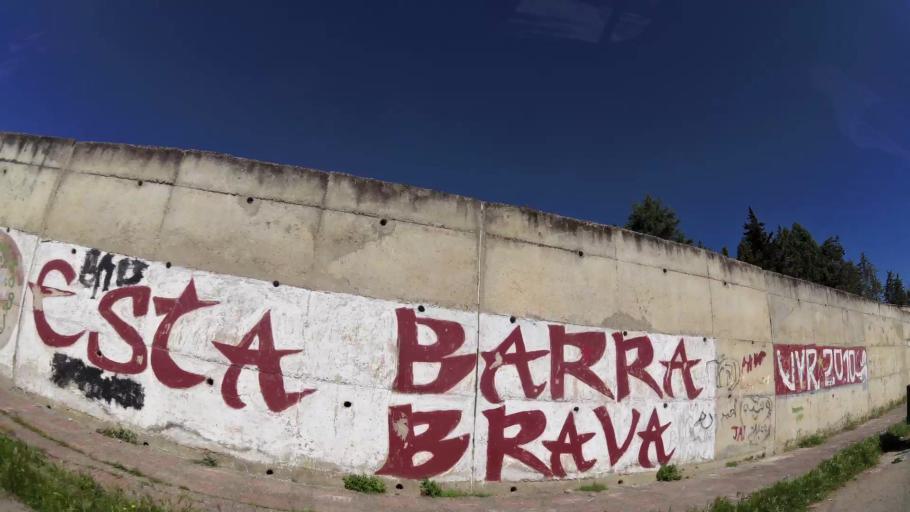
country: MA
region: Meknes-Tafilalet
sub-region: Meknes
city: Meknes
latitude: 33.9056
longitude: -5.5439
